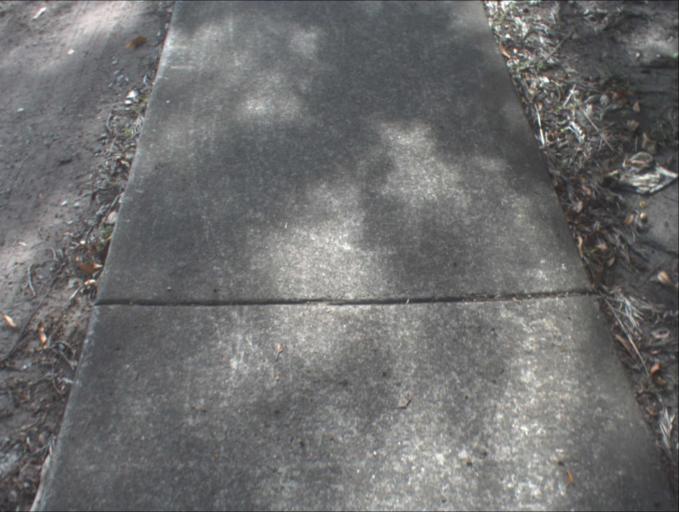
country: AU
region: Queensland
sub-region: Logan
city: Woodridge
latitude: -27.6338
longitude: 153.1023
